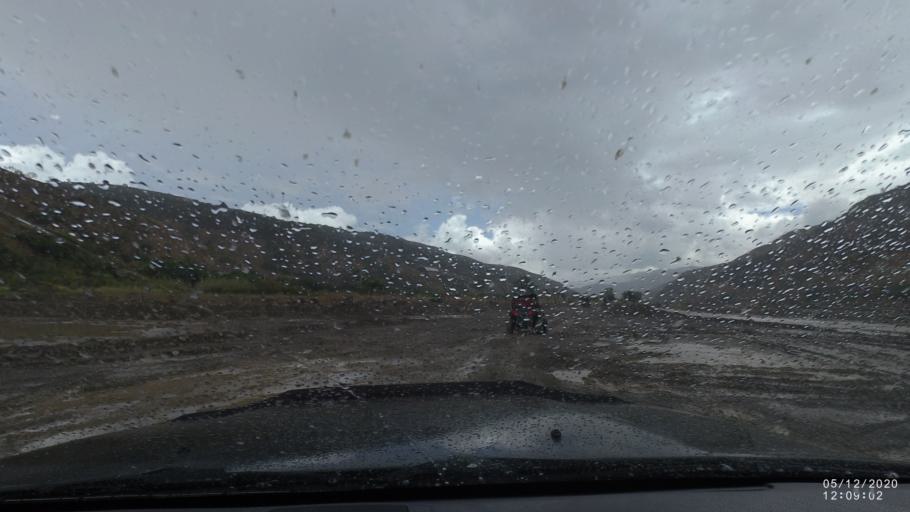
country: BO
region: Cochabamba
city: Sipe Sipe
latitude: -17.5698
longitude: -66.3688
